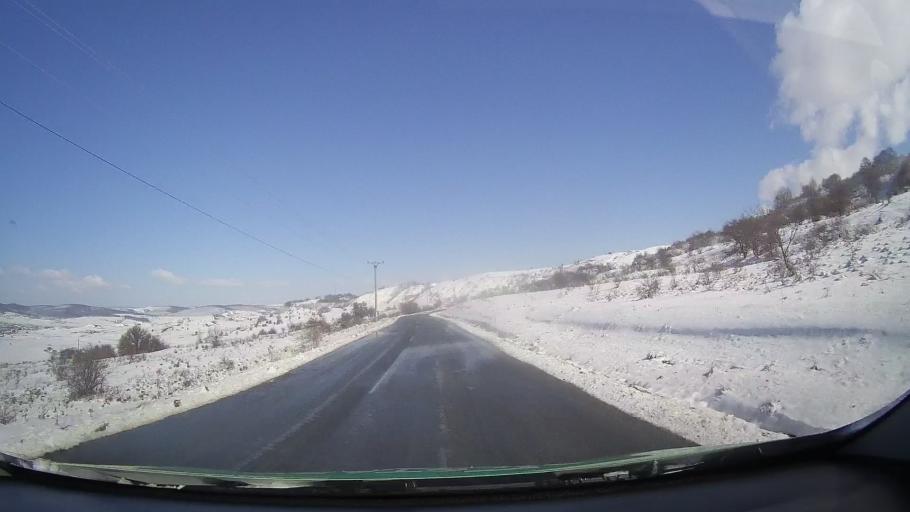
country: RO
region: Sibiu
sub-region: Comuna Avrig
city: Avrig
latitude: 45.7770
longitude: 24.3690
